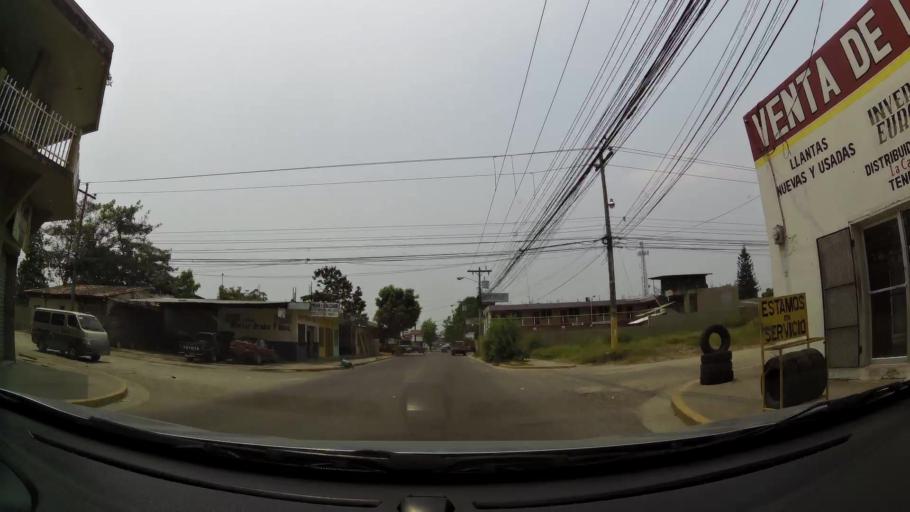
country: HN
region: Yoro
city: El Progreso
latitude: 15.3973
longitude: -87.8089
